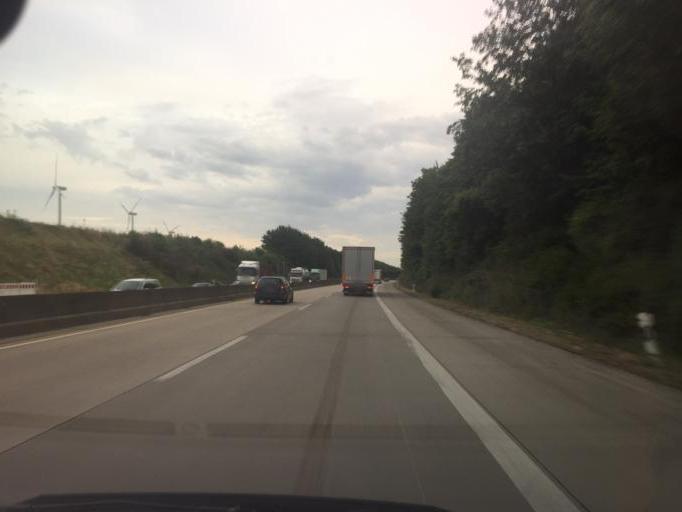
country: DE
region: North Rhine-Westphalia
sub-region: Regierungsbezirk Koln
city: Titz
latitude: 51.0273
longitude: 6.4811
